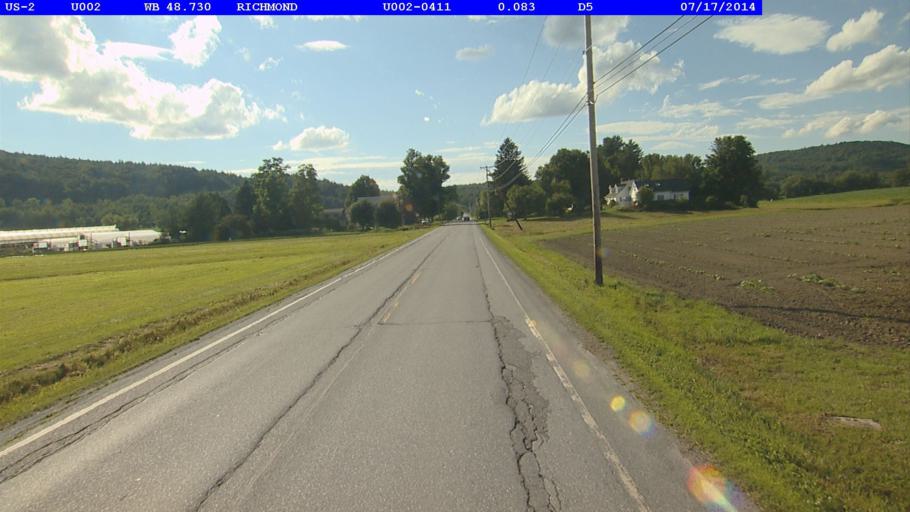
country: US
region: Vermont
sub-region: Chittenden County
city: Williston
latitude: 44.4284
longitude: -73.0270
